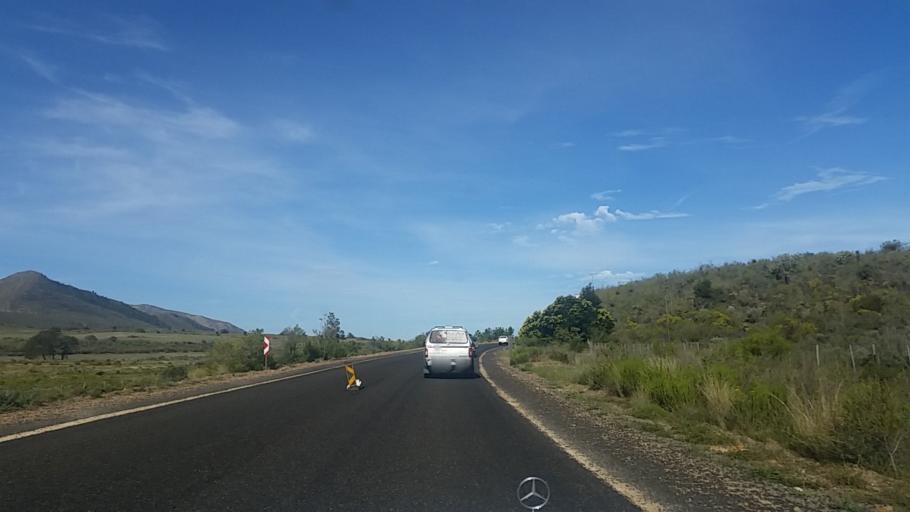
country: ZA
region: Western Cape
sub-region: Eden District Municipality
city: George
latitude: -33.8259
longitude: 22.3932
